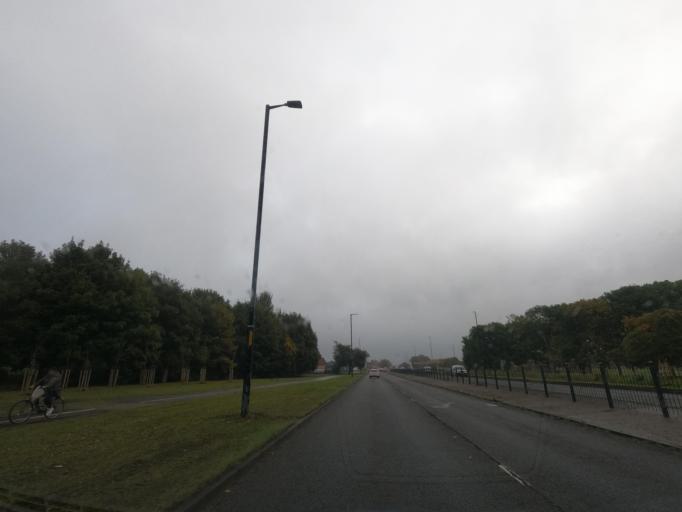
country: GB
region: England
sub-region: Middlesbrough
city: Middlesbrough
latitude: 54.5686
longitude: -1.2027
